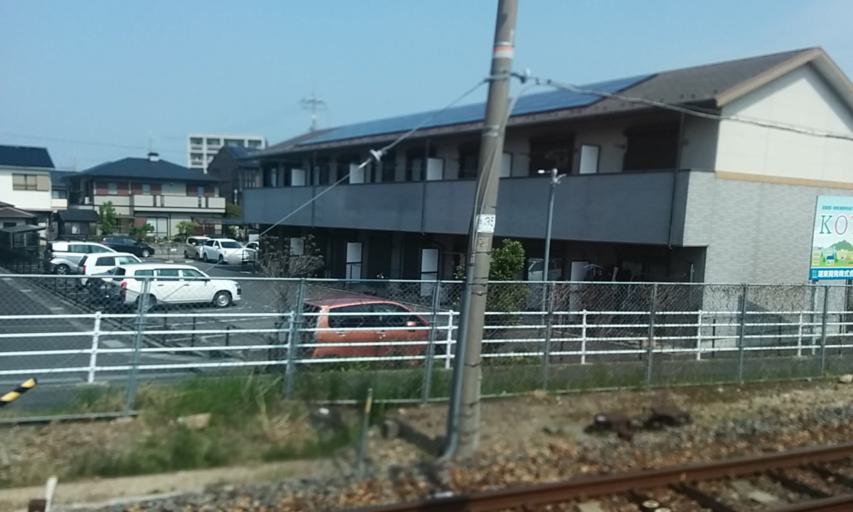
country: JP
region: Shiga Prefecture
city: Moriyama
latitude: 35.0666
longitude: 136.0197
